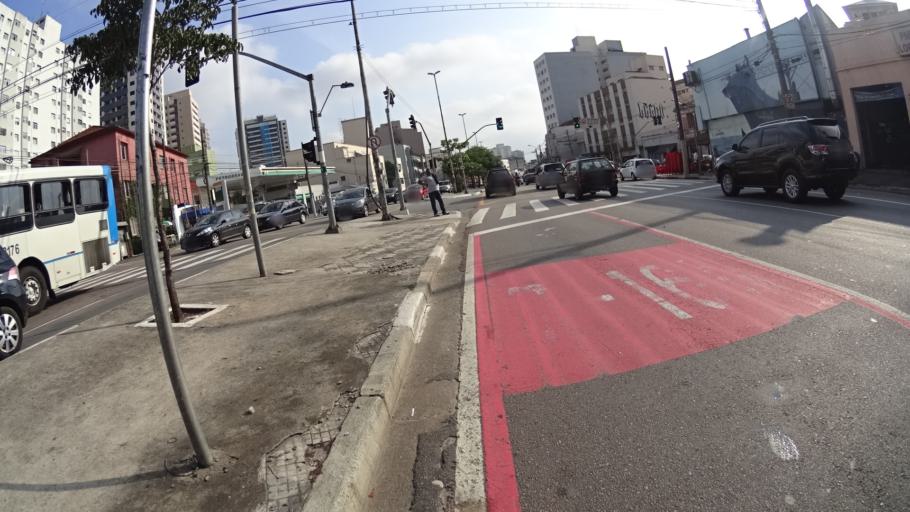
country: BR
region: Sao Paulo
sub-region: Sao Paulo
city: Sao Paulo
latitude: -23.5895
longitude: -46.6348
